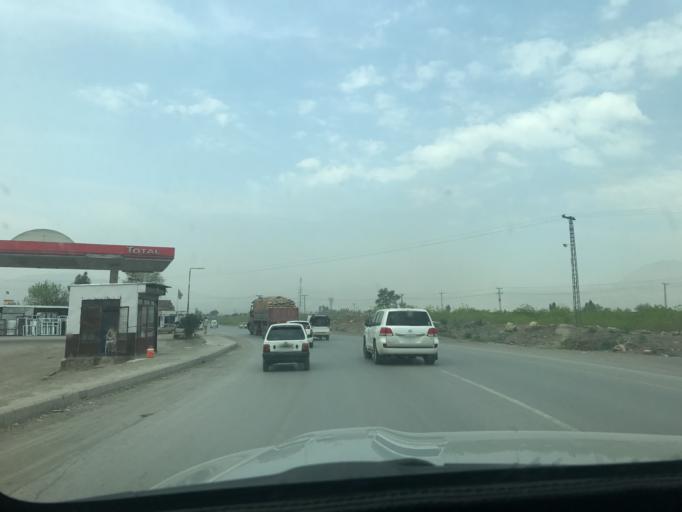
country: PK
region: Khyber Pakhtunkhwa
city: Peshawar
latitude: 34.0016
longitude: 71.3971
